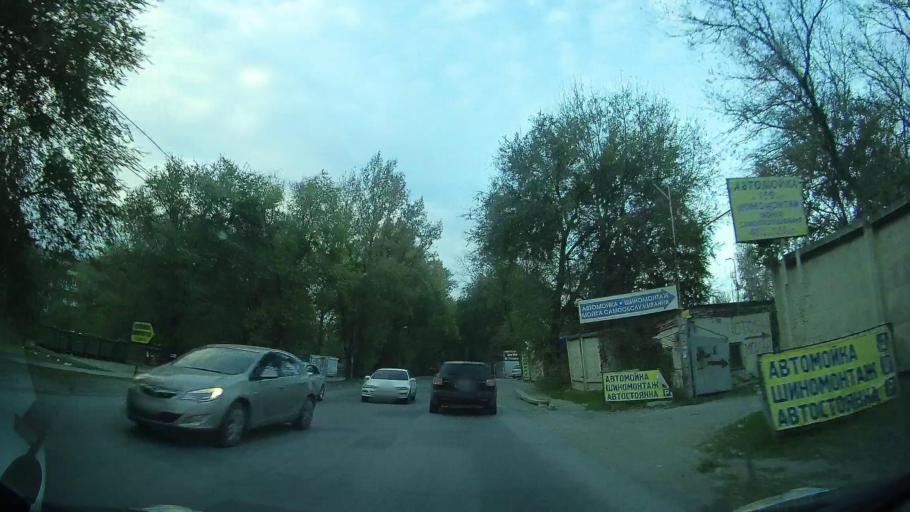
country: RU
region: Rostov
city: Severnyy
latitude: 47.2697
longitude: 39.6610
